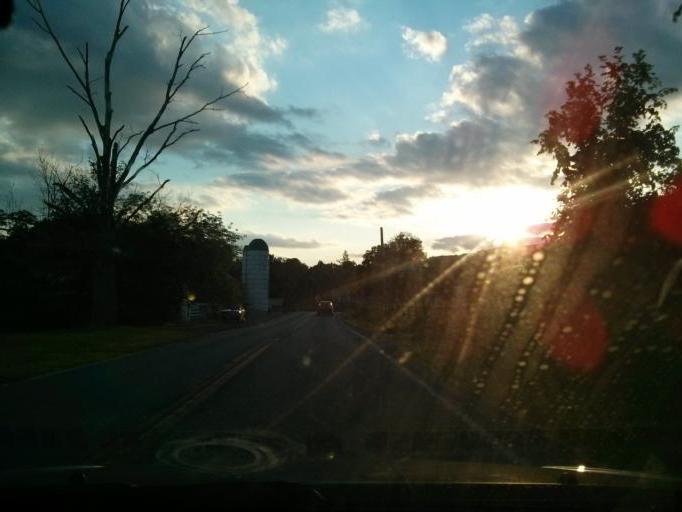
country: US
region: Pennsylvania
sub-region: Centre County
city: Park Forest Village
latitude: 40.8339
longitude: -77.9328
